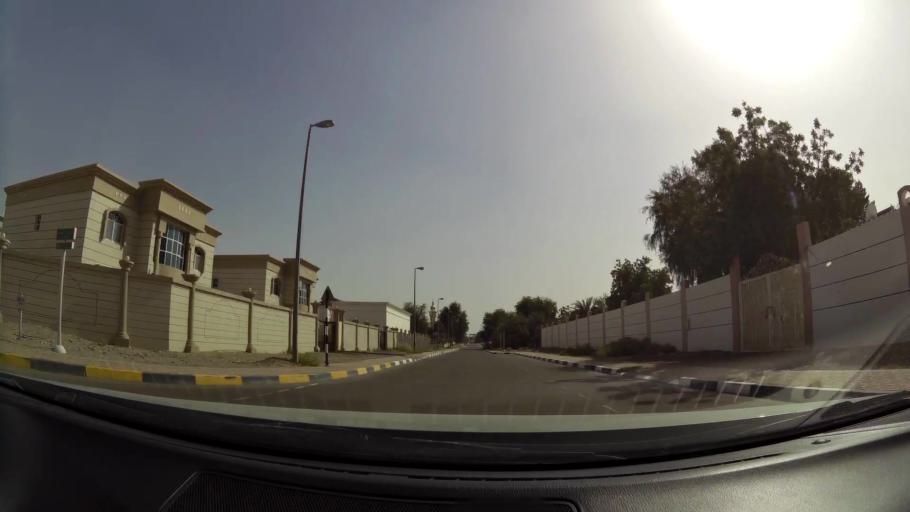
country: AE
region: Abu Dhabi
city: Al Ain
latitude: 24.2478
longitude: 55.6853
